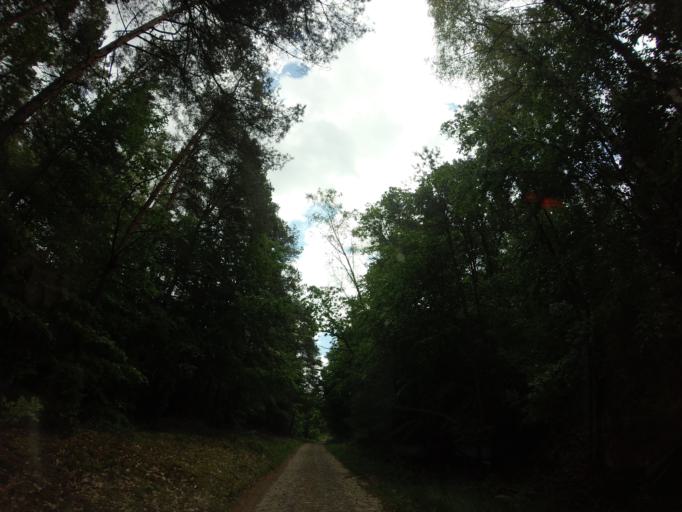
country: PL
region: West Pomeranian Voivodeship
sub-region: Powiat drawski
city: Kalisz Pomorski
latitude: 53.1634
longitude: 15.9068
